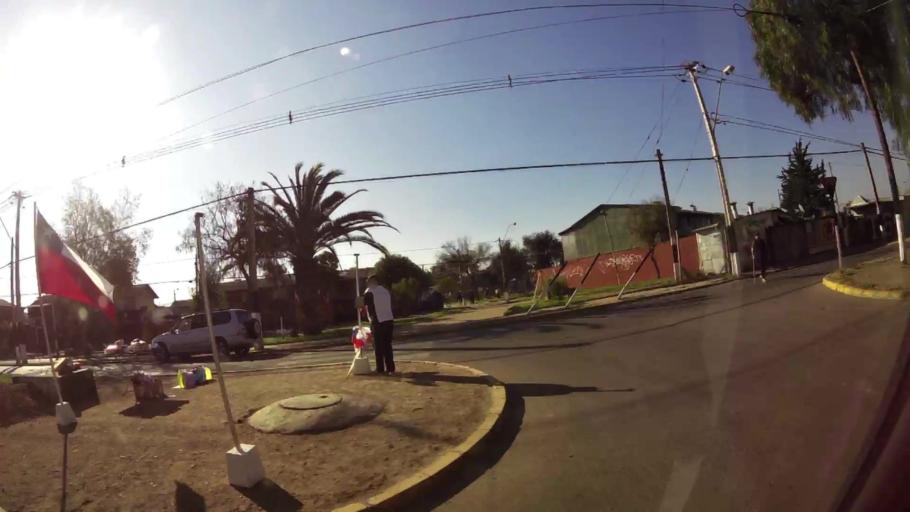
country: CL
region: Santiago Metropolitan
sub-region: Provincia de Santiago
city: Lo Prado
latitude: -33.4899
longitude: -70.7673
